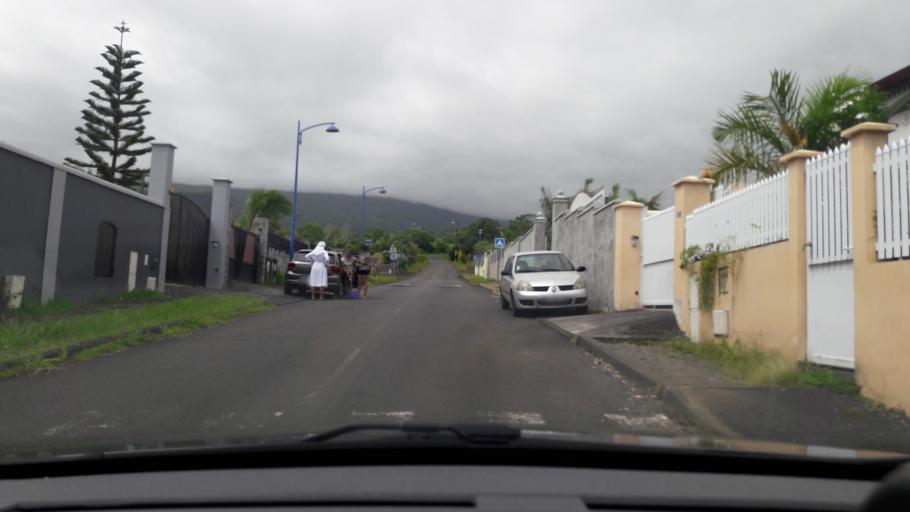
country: RE
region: Reunion
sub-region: Reunion
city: Saint-Benoit
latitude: -21.0941
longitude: 55.7026
